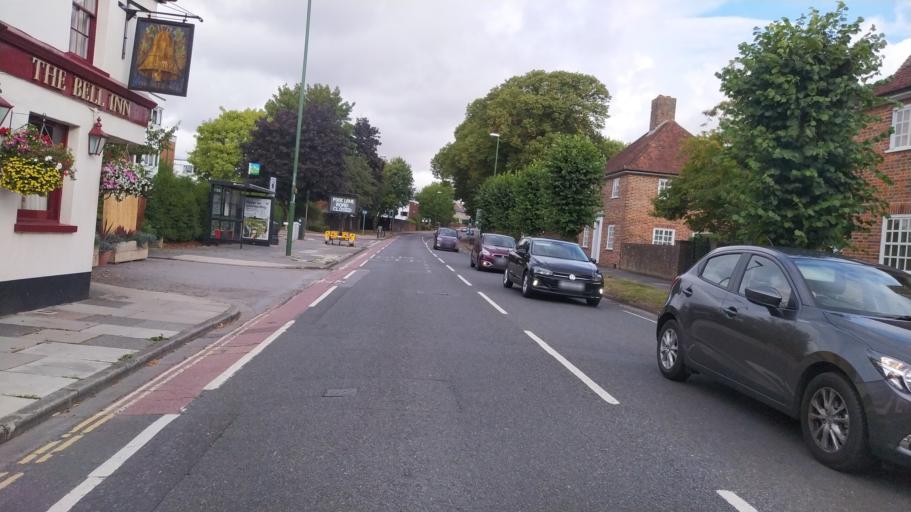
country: GB
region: England
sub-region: West Sussex
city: Chichester
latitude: 50.8421
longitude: -0.7790
